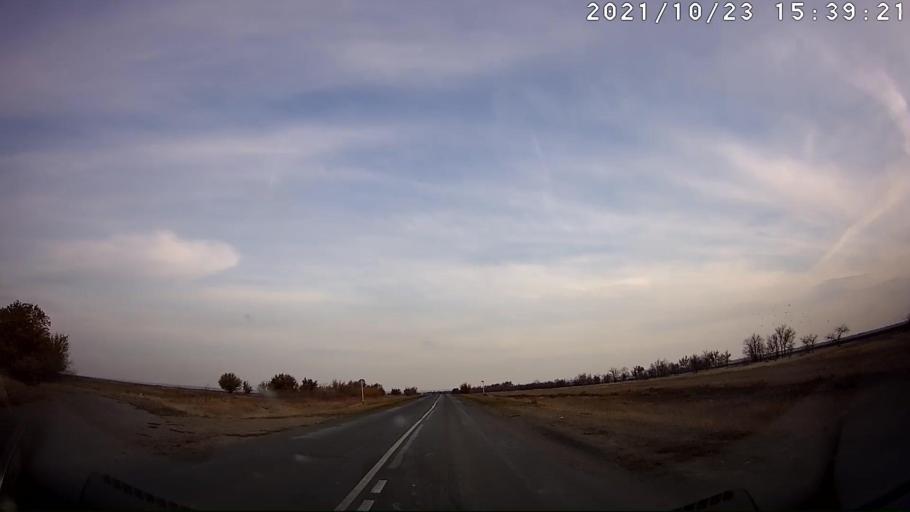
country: RU
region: Volgograd
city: Bereslavka
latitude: 48.1247
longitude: 44.1264
